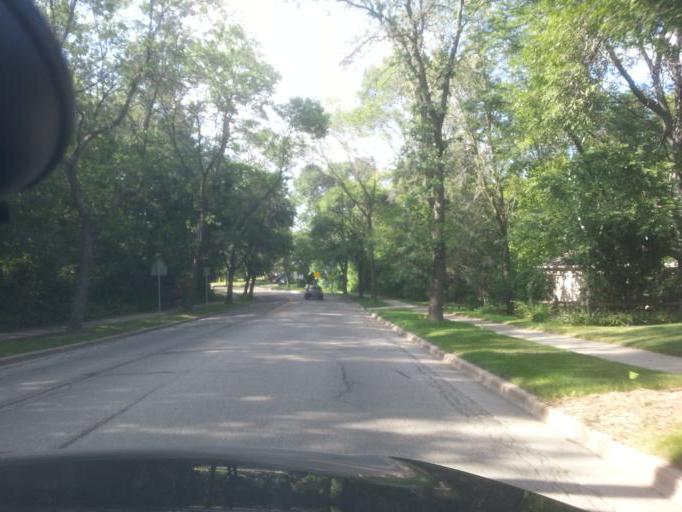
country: US
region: Wisconsin
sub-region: Dane County
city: Middleton
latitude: 43.0688
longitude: -89.4932
